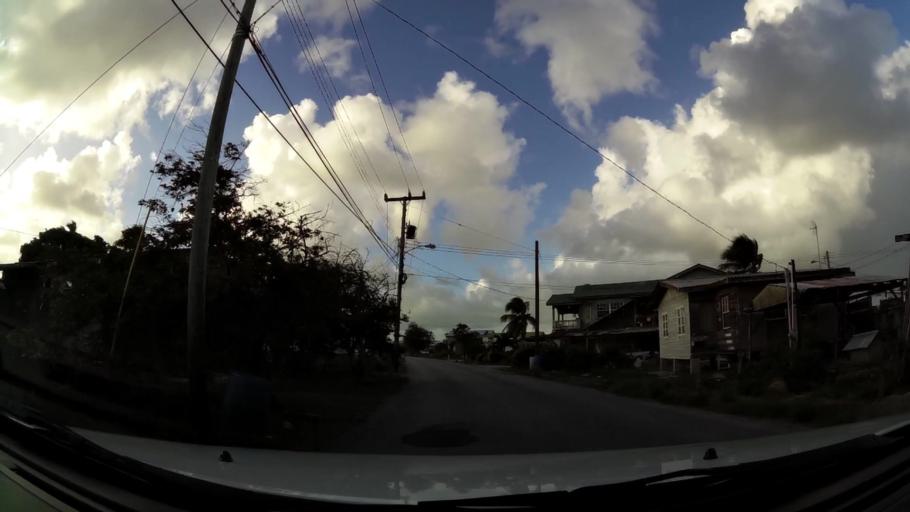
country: BB
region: Saint Philip
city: Crane
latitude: 13.1071
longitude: -59.4694
